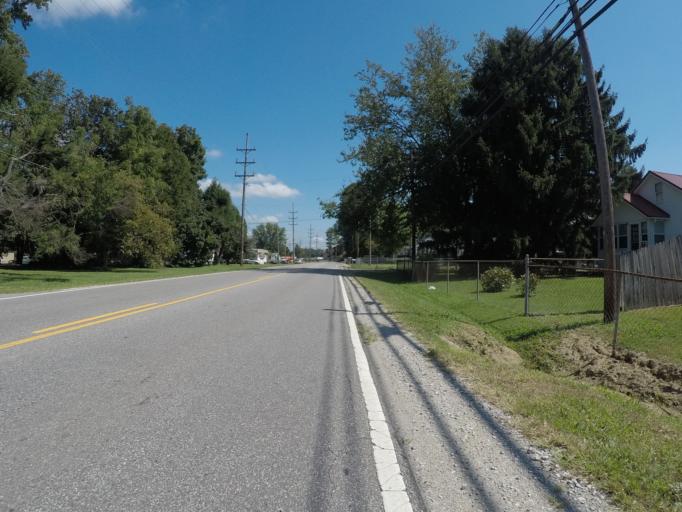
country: US
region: Ohio
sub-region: Lawrence County
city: Burlington
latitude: 38.4093
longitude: -82.5221
